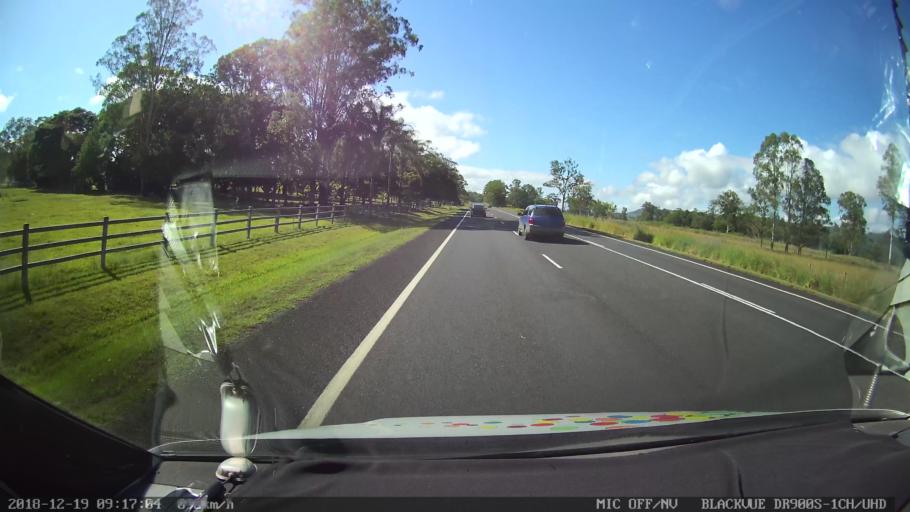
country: AU
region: New South Wales
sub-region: Kyogle
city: Kyogle
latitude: -28.5286
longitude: 152.9723
